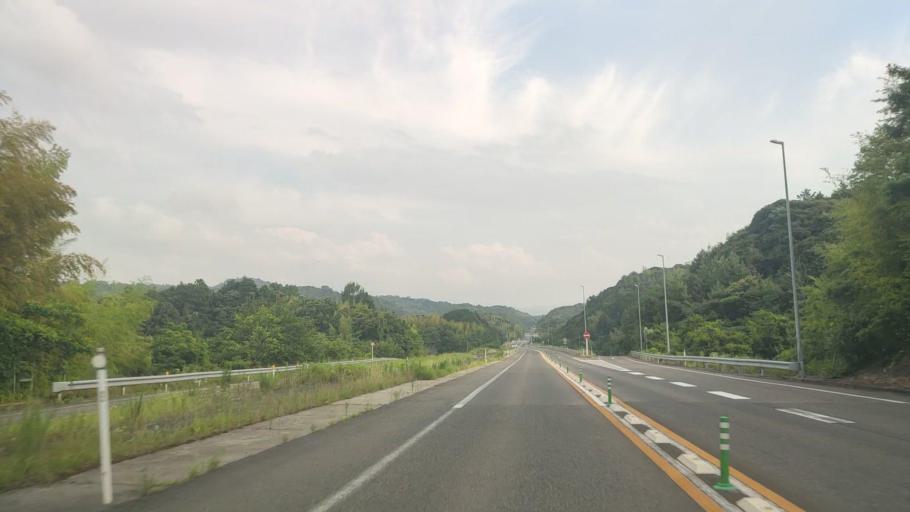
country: JP
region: Tottori
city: Kurayoshi
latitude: 35.4678
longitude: 133.8081
